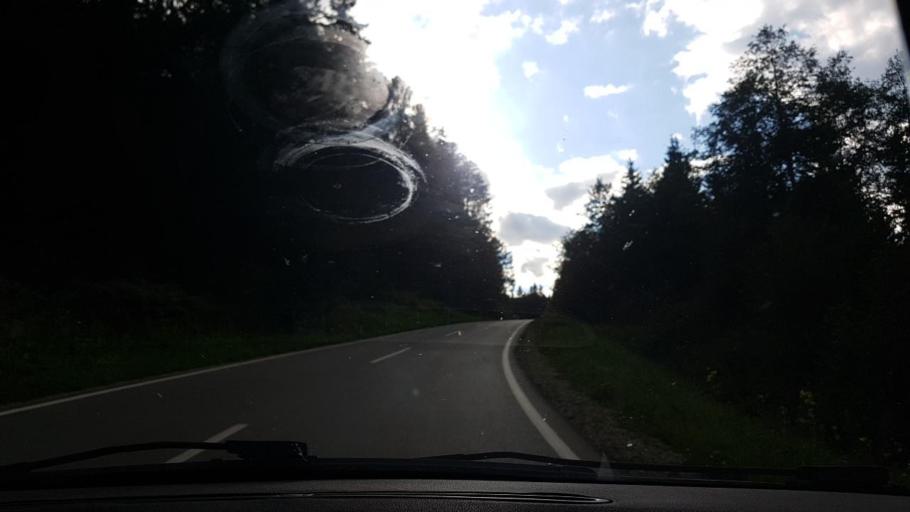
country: AT
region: Salzburg
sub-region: Politischer Bezirk Tamsweg
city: Sankt Michael im Lungau
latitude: 47.0853
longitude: 13.6321
